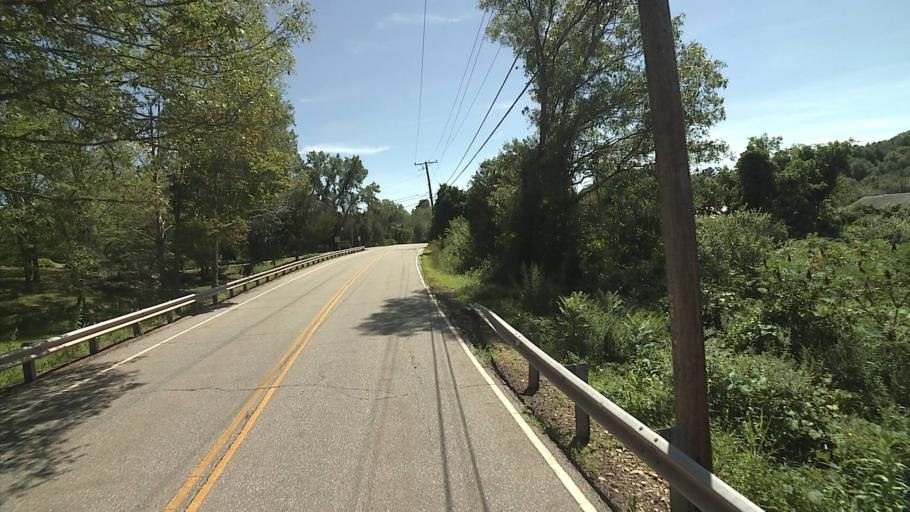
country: US
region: Connecticut
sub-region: New London County
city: Baltic
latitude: 41.6782
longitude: -72.0841
